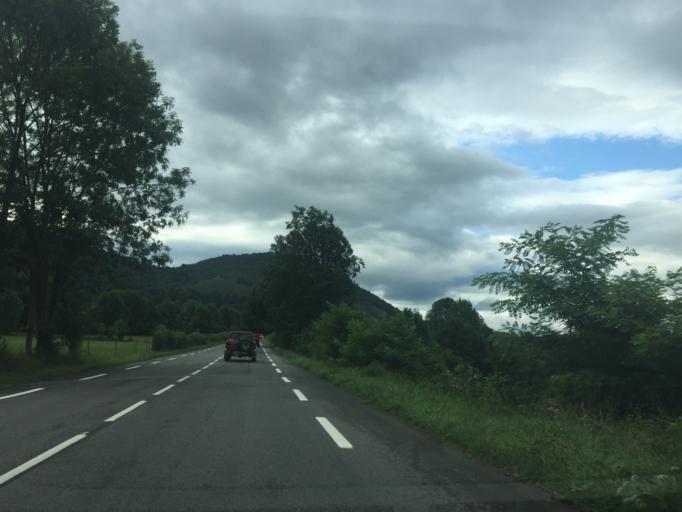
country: FR
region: Midi-Pyrenees
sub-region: Departement des Hautes-Pyrenees
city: La Barthe-de-Neste
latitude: 43.0066
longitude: 0.3774
